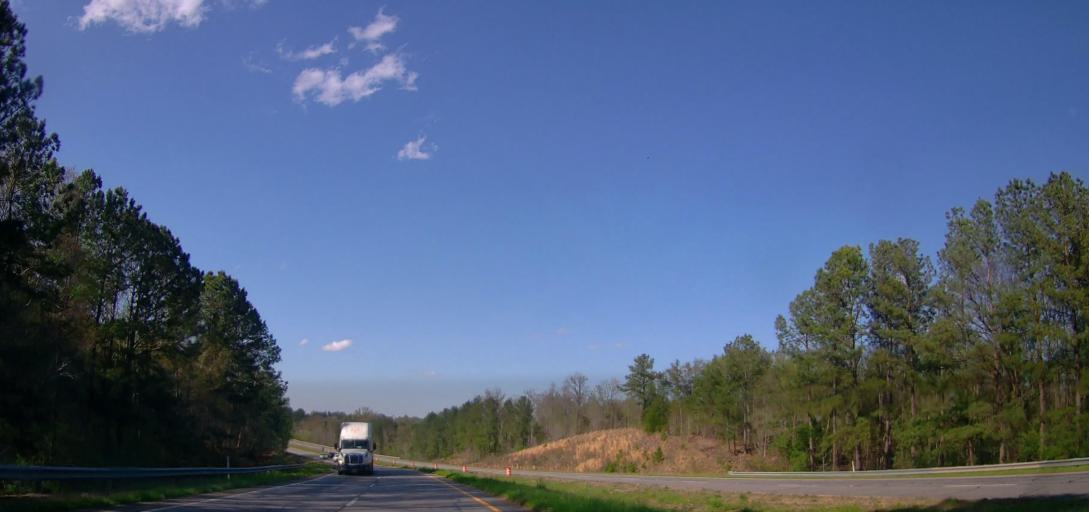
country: US
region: Georgia
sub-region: Baldwin County
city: Milledgeville
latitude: 33.0676
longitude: -83.2491
